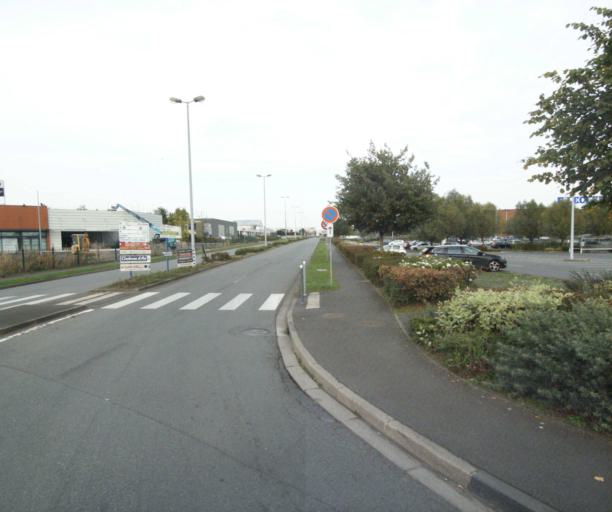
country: FR
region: Nord-Pas-de-Calais
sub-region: Departement du Nord
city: Seclin
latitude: 50.5494
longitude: 3.0516
